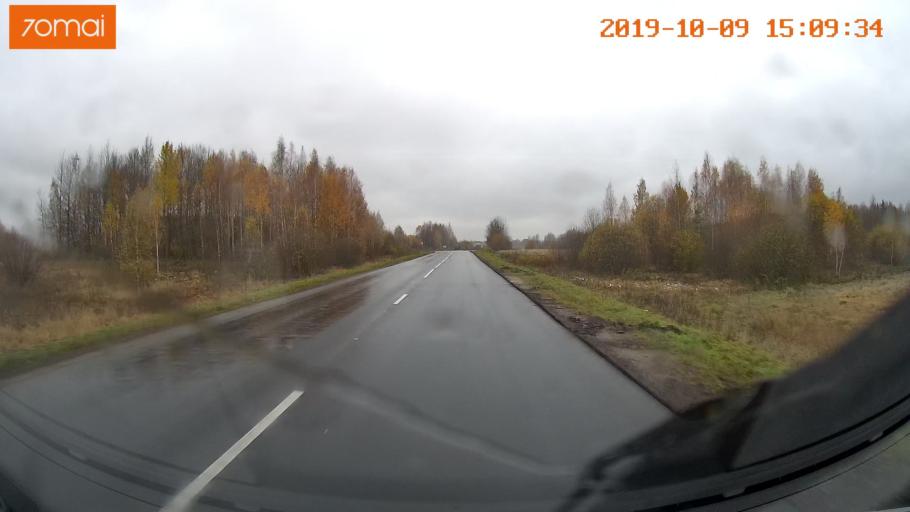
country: RU
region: Kostroma
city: Susanino
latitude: 58.1896
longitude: 41.6496
